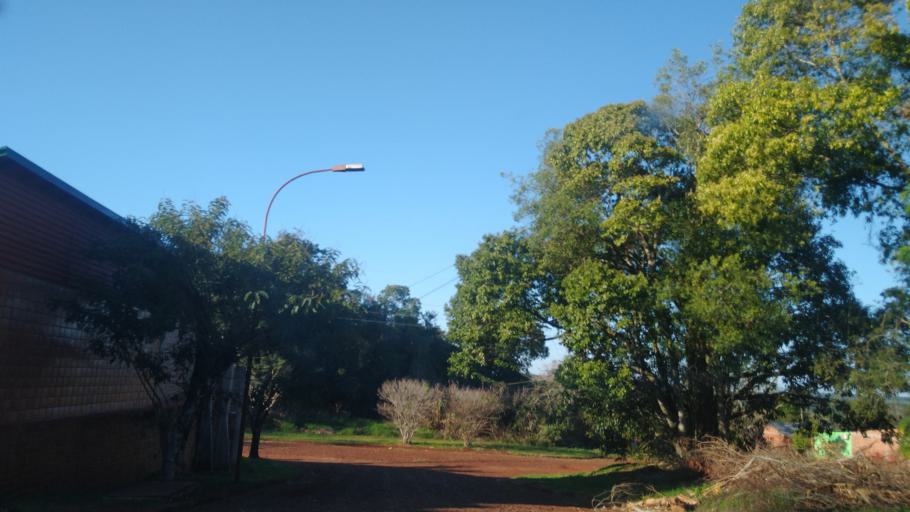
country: AR
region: Misiones
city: Puerto Libertad
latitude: -25.9726
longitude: -54.5557
